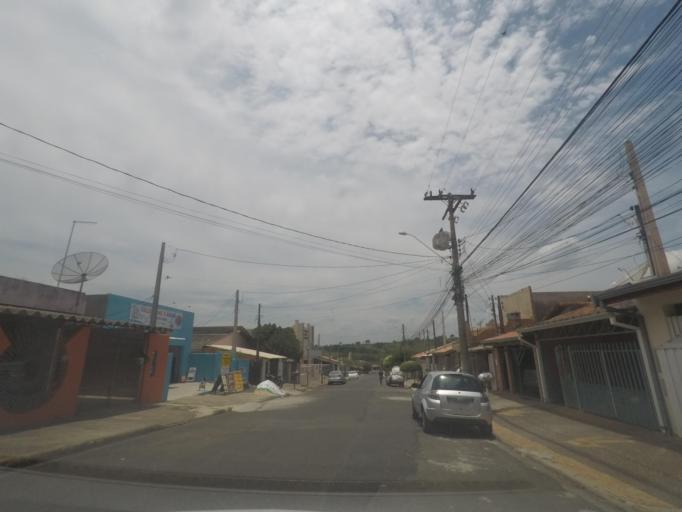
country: BR
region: Sao Paulo
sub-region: Nova Odessa
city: Nova Odessa
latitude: -22.7933
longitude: -47.2776
